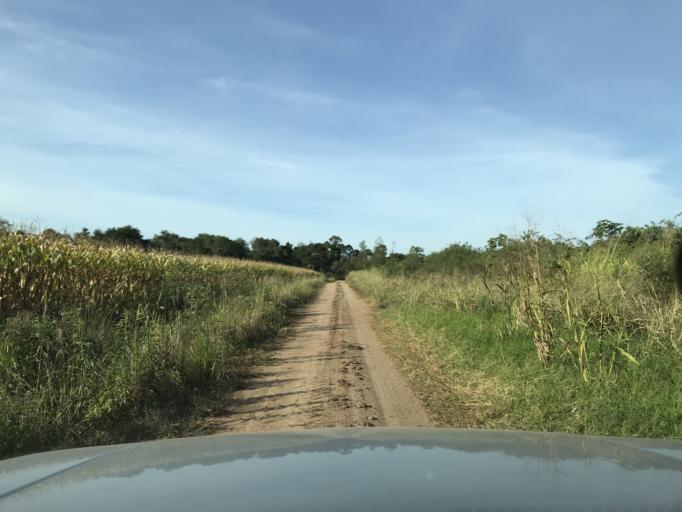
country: BR
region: Parana
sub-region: Palotina
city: Palotina
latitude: -24.2512
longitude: -53.7539
